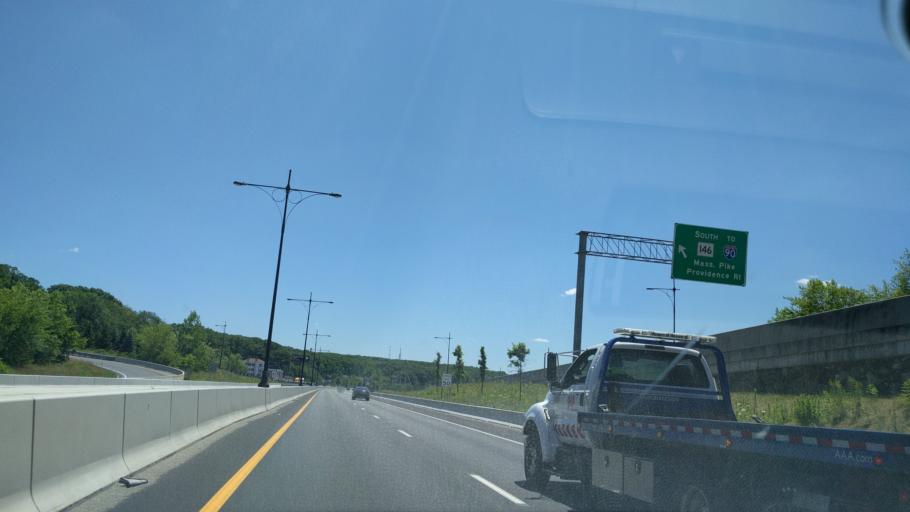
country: US
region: Massachusetts
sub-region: Worcester County
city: Sunderland
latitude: 42.2361
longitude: -71.7932
